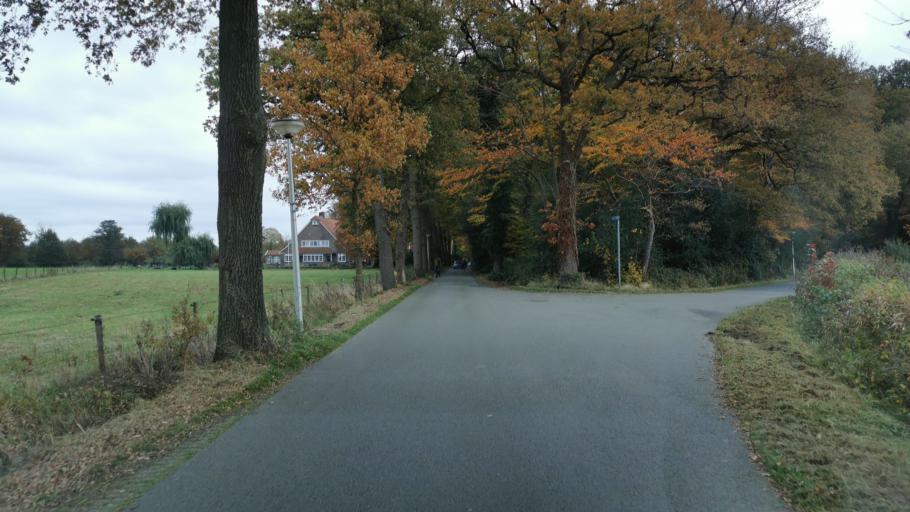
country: NL
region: Overijssel
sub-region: Gemeente Enschede
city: Enschede
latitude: 52.2083
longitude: 6.9207
